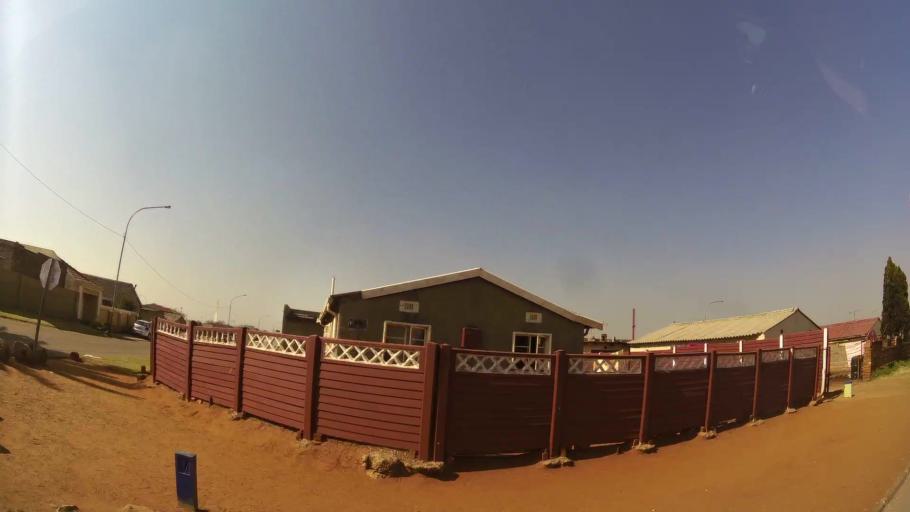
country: ZA
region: Gauteng
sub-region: Ekurhuleni Metropolitan Municipality
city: Benoni
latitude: -26.2240
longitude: 28.3028
